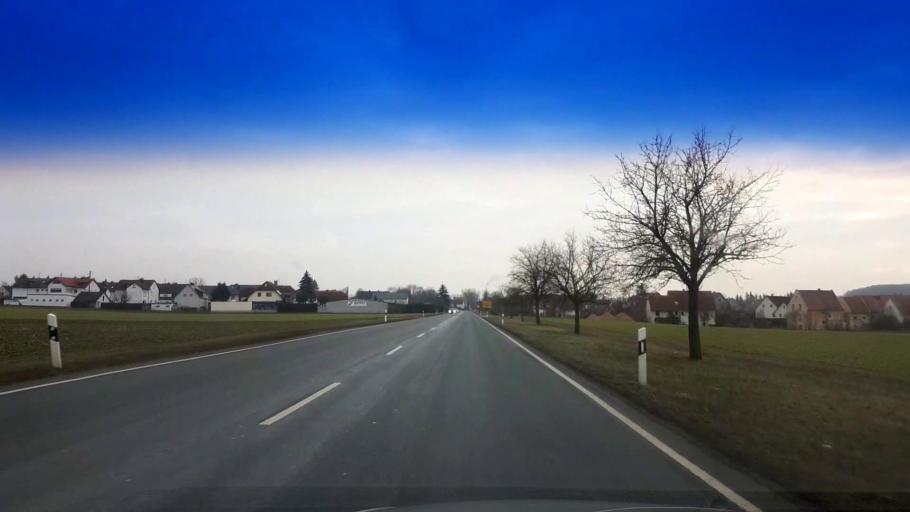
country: DE
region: Bavaria
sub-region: Upper Franconia
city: Altendorf
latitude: 49.8036
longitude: 11.0074
